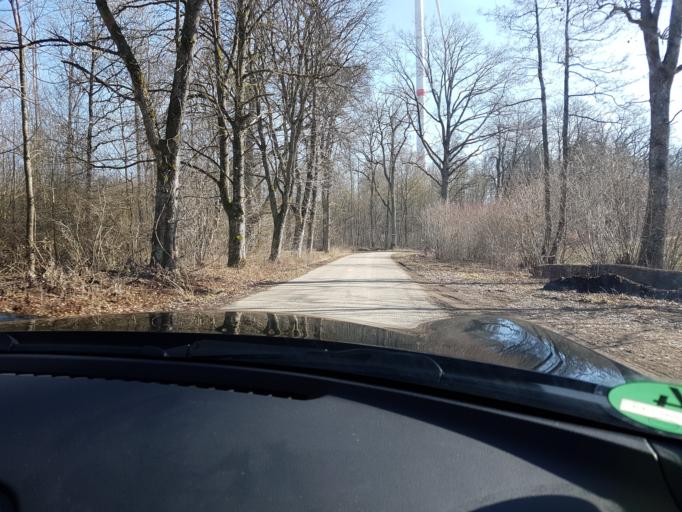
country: DE
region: Baden-Wuerttemberg
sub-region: Regierungsbezirk Stuttgart
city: Langenburg
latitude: 49.2797
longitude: 9.8786
